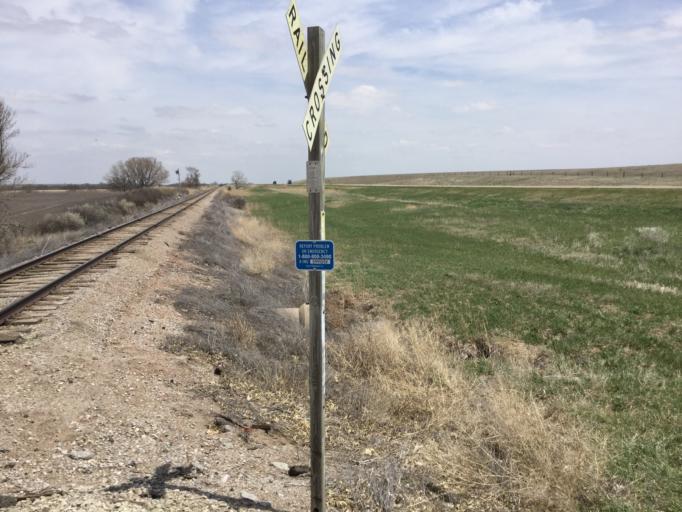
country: US
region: Kansas
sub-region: Norton County
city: Norton
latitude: 39.7483
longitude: -100.1524
